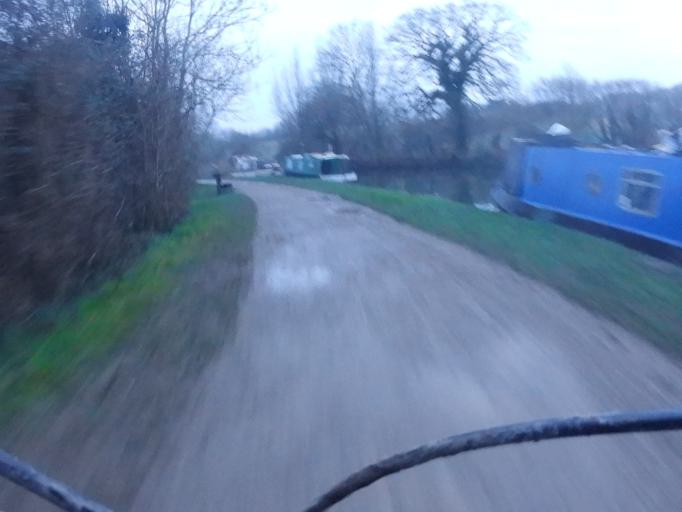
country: GB
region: England
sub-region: Bath and North East Somerset
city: Bath
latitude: 51.3952
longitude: -2.3165
